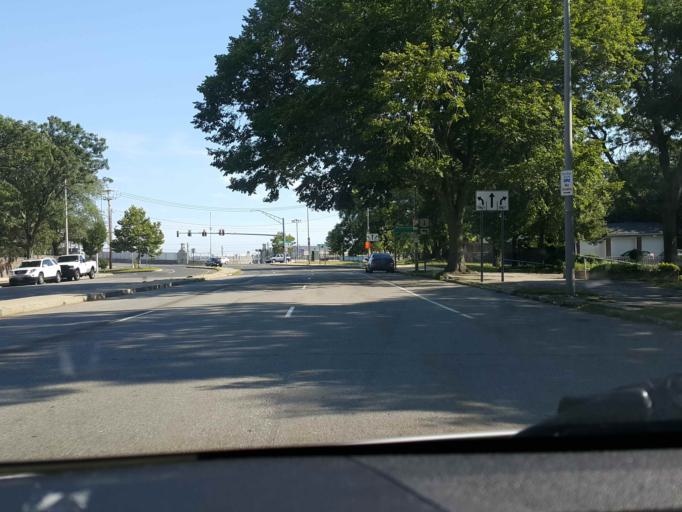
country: US
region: Connecticut
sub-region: New Haven County
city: New Haven
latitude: 41.2974
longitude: -72.9289
